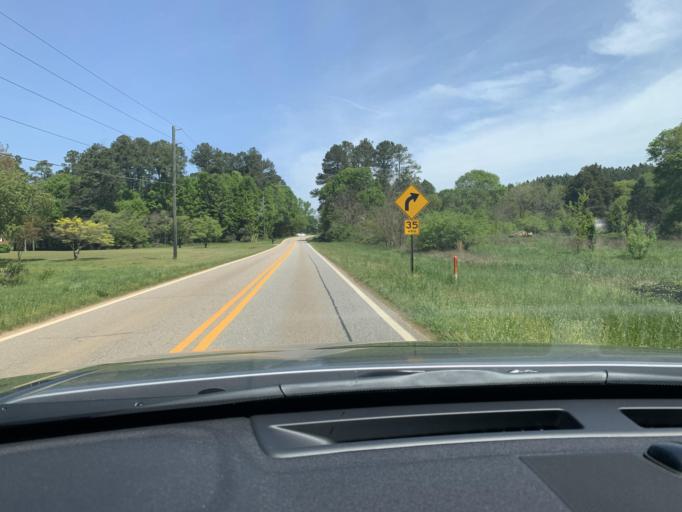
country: US
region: Georgia
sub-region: Oconee County
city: Bogart
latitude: 33.9188
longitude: -83.5622
